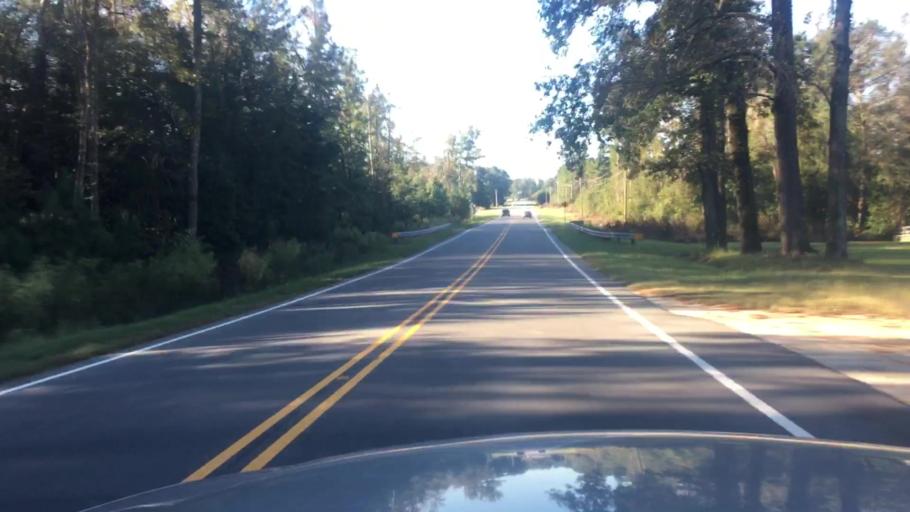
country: US
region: North Carolina
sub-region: Cumberland County
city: Spring Lake
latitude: 35.2593
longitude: -78.9237
